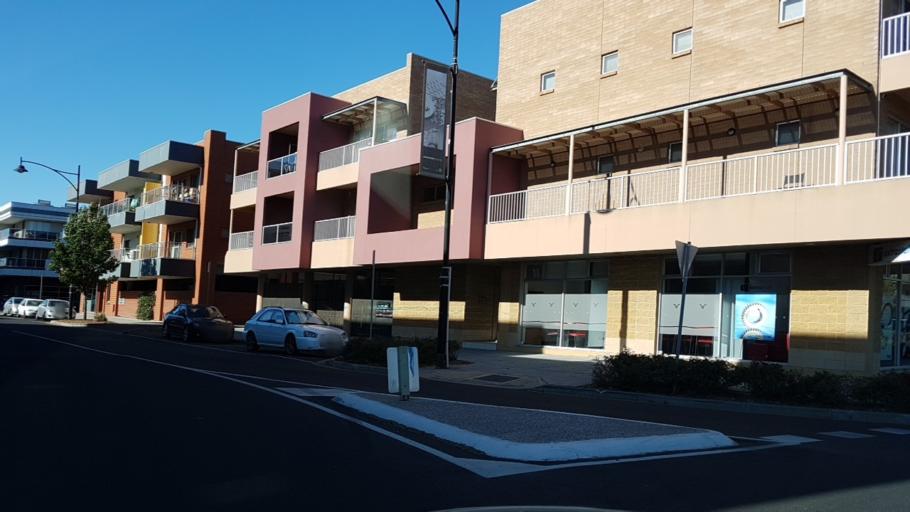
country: AU
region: South Australia
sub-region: Salisbury
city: Ingle Farm
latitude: -34.8080
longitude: 138.6148
